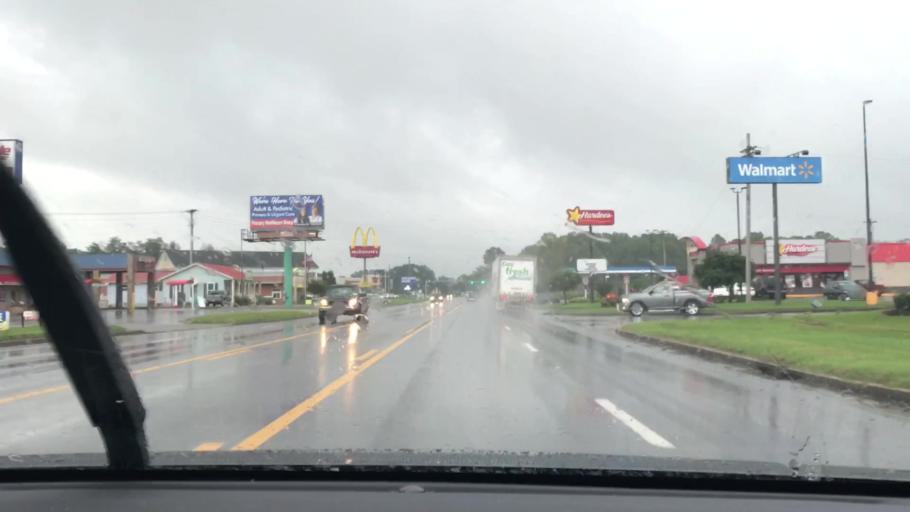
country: US
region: Tennessee
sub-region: Macon County
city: Lafayette
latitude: 36.5211
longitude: -86.0370
